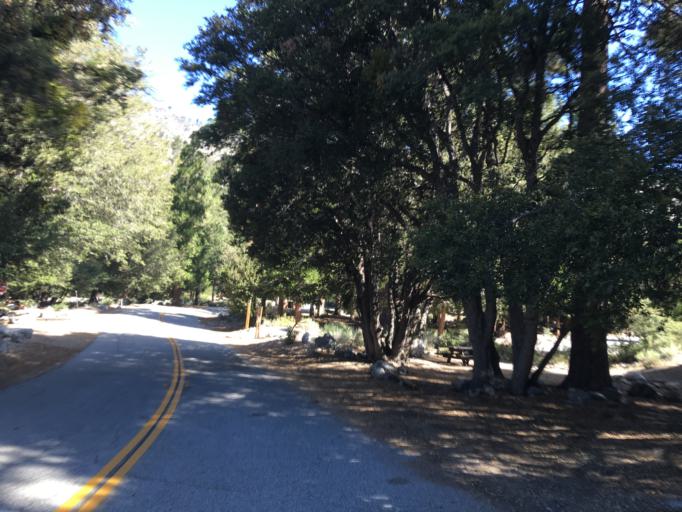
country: US
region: California
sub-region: Los Angeles County
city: Glendora
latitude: 34.3263
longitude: -117.8346
